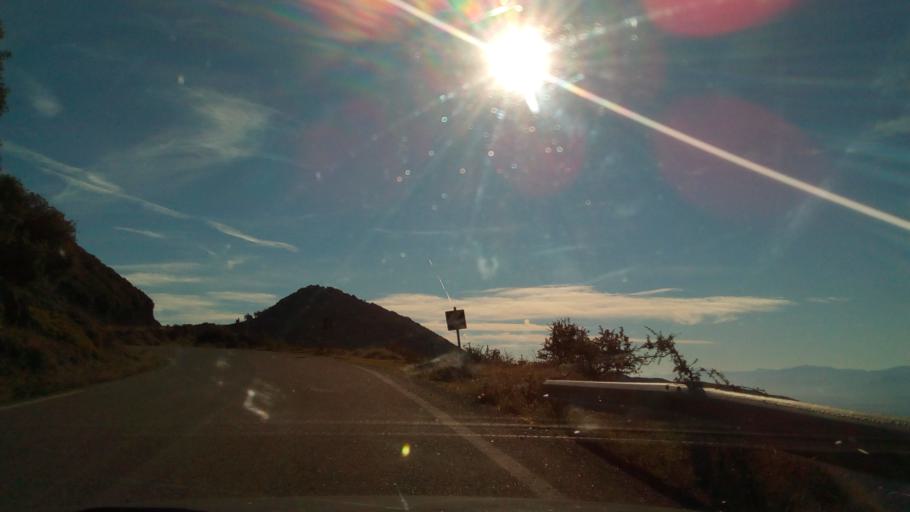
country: GR
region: West Greece
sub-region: Nomos Aitolias kai Akarnanias
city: Nafpaktos
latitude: 38.4842
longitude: 21.8606
